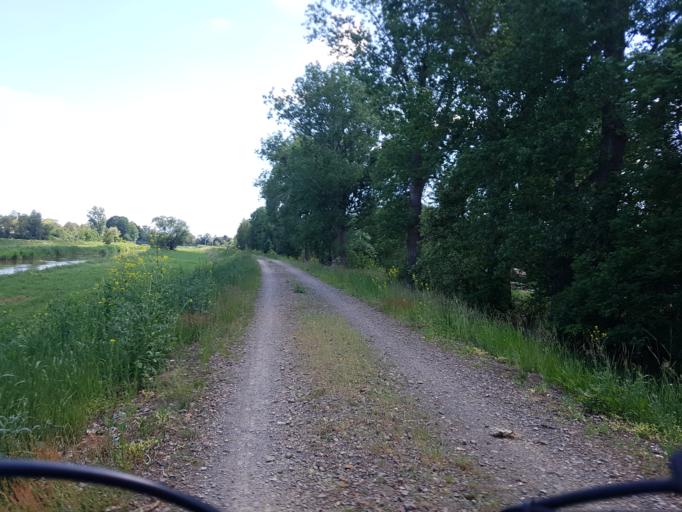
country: DE
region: Brandenburg
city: Bad Liebenwerda
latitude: 51.5251
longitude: 13.3845
